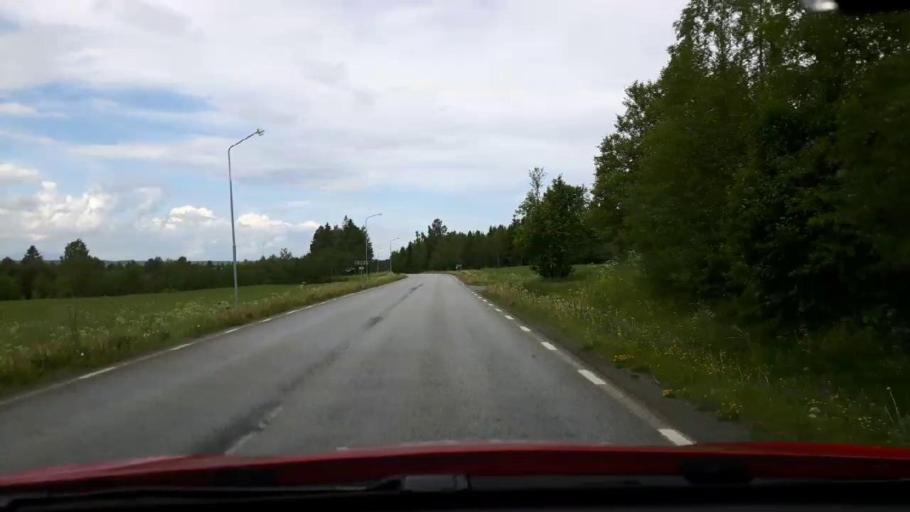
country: SE
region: Jaemtland
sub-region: Bergs Kommun
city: Hoverberg
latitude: 63.0198
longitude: 14.4849
